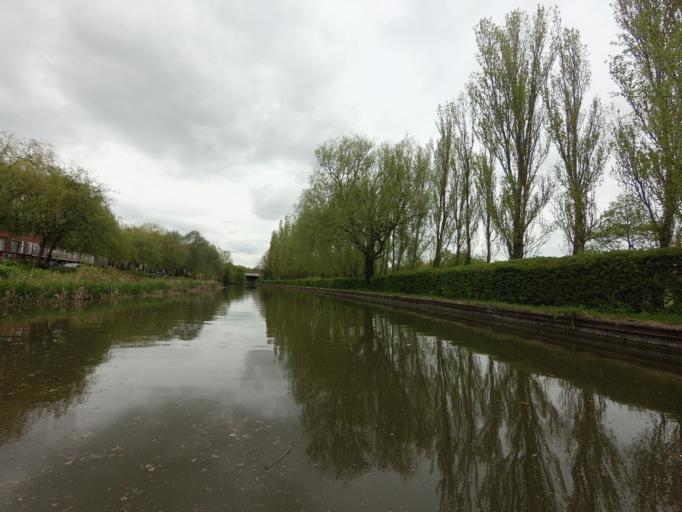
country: GB
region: England
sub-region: Milton Keynes
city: Milton Keynes
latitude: 52.0353
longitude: -0.7305
